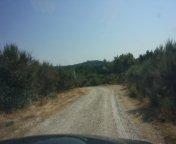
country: PT
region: Viseu
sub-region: Sernancelhe
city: Sernancelhe
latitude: 40.9323
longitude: -7.5122
